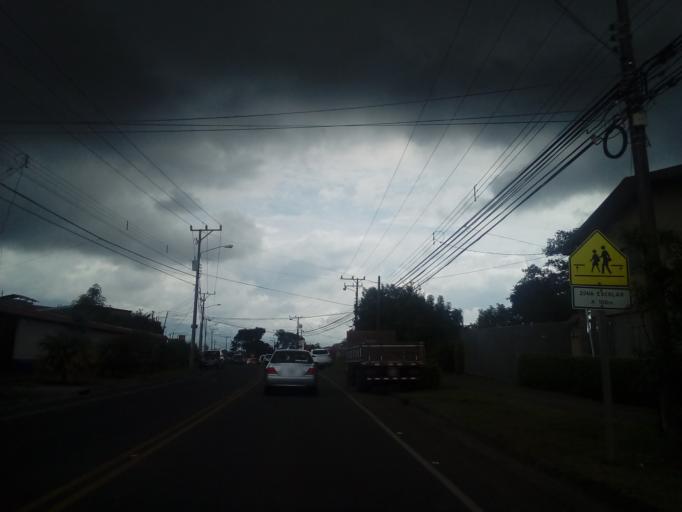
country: CR
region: Heredia
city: Angeles
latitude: 9.9910
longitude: -84.0569
